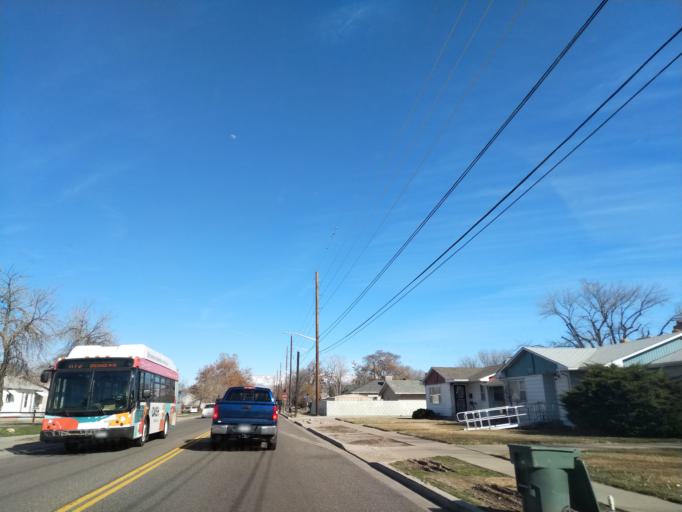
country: US
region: Colorado
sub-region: Mesa County
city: Grand Junction
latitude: 39.0846
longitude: -108.5490
